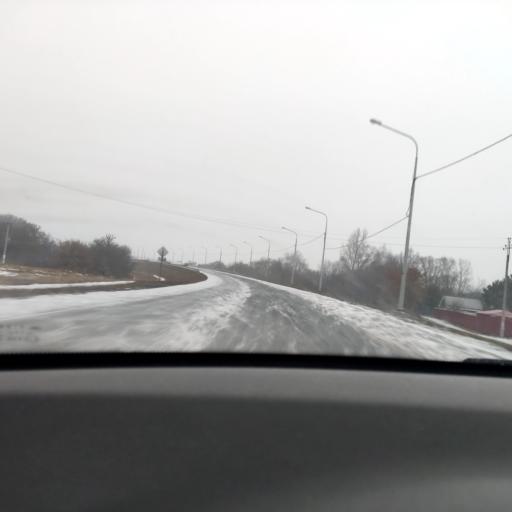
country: RU
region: Samara
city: Krasnoarmeyskoye
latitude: 52.8993
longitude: 49.9622
